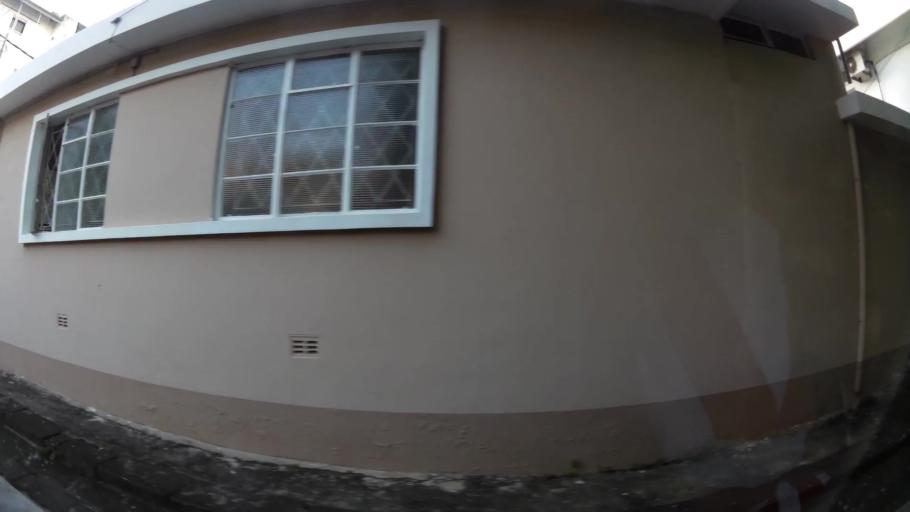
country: MU
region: Port Louis
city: Port Louis
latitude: -20.1710
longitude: 57.5004
